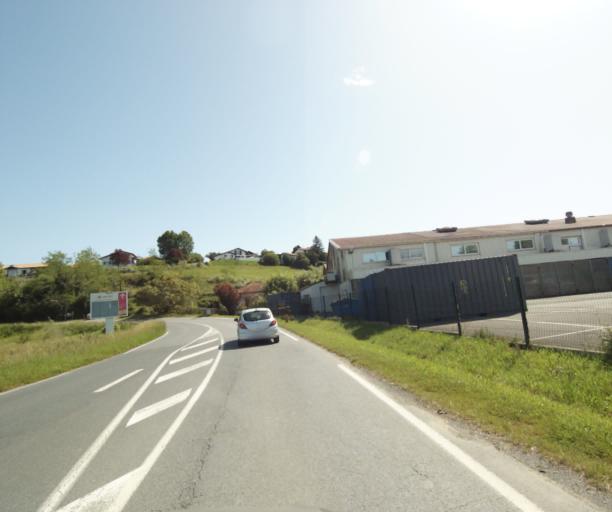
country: FR
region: Aquitaine
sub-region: Departement des Pyrenees-Atlantiques
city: Villefranque
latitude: 43.4664
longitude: -1.4494
